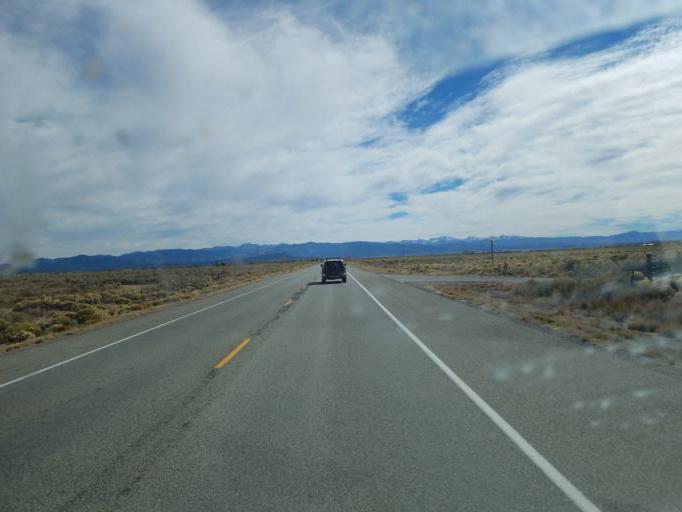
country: US
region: Colorado
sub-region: Costilla County
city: San Luis
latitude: 37.4464
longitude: -105.5365
